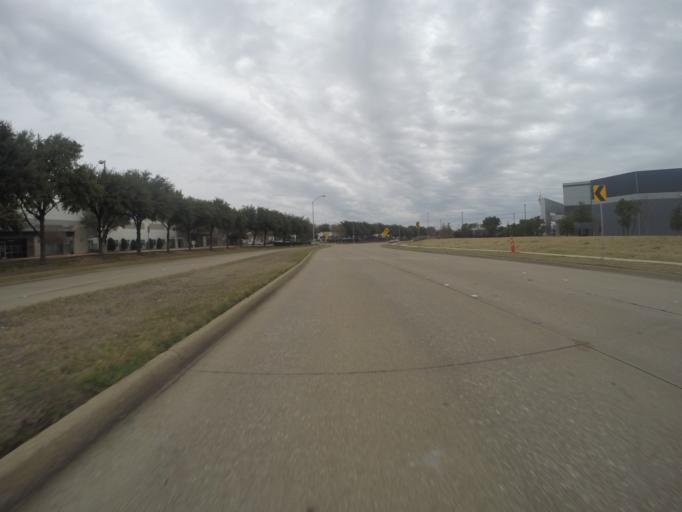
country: US
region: Texas
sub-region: Collin County
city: Saint Paul
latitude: 33.0417
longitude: -96.5685
